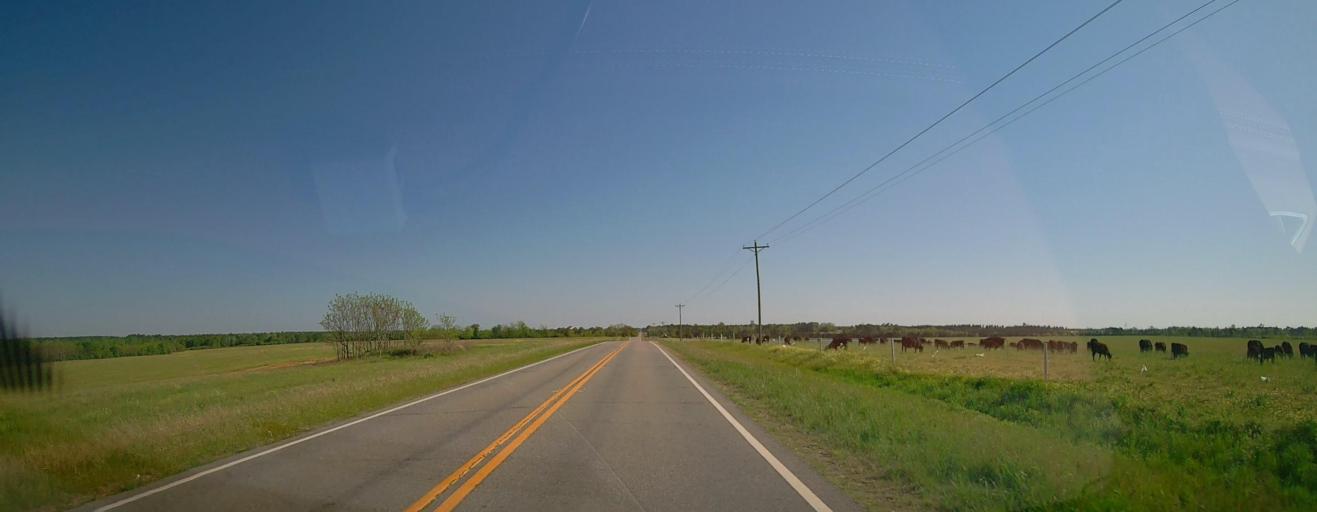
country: US
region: Georgia
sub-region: Wilcox County
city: Rochelle
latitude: 31.8845
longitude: -83.4887
